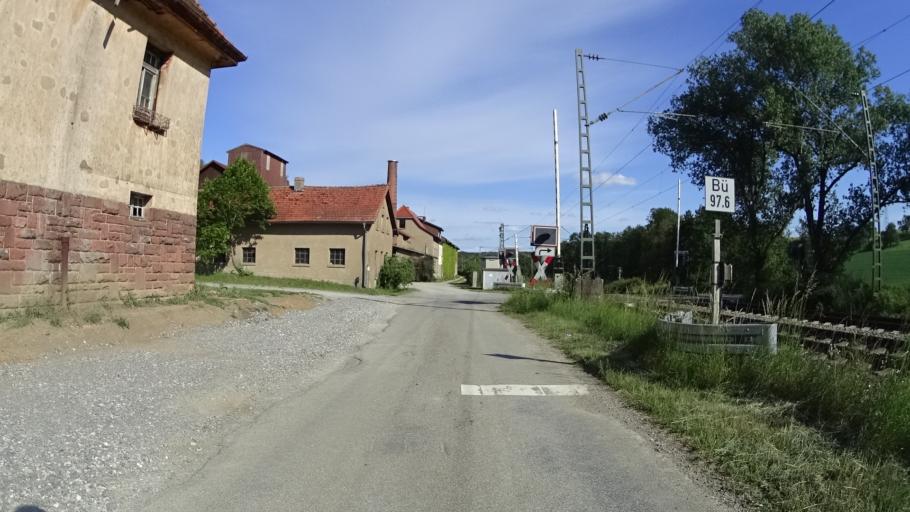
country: DE
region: Baden-Wuerttemberg
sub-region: Regierungsbezirk Stuttgart
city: Buch am Ahorn
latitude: 49.5205
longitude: 9.5854
